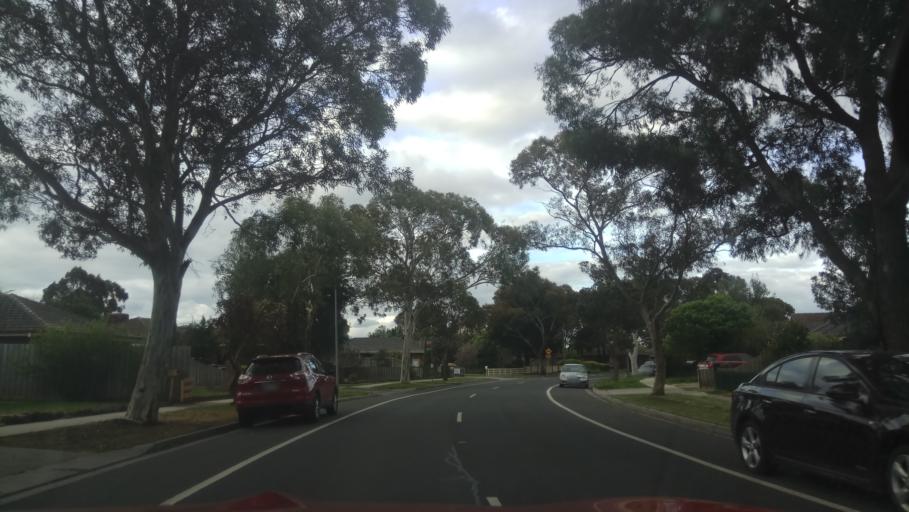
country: AU
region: Victoria
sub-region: Casey
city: Cranbourne North
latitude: -38.0767
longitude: 145.2633
